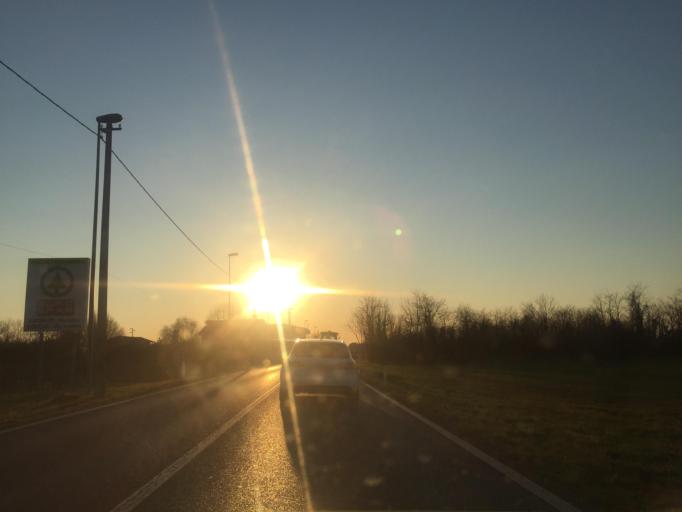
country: IT
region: Friuli Venezia Giulia
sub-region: Provincia di Gorizia
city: Mossa
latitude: 45.9334
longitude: 13.5382
